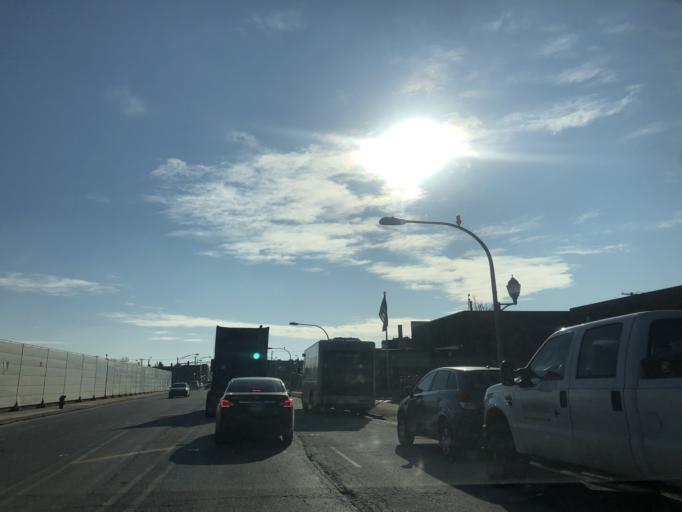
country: US
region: Illinois
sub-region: Cook County
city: Stickney
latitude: 41.7794
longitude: -87.7618
